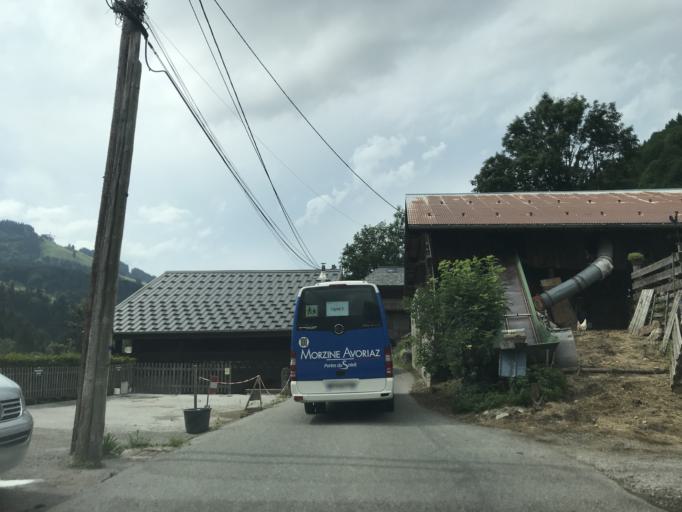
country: FR
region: Rhone-Alpes
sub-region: Departement de la Haute-Savoie
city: Morzine
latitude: 46.1632
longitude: 6.7217
